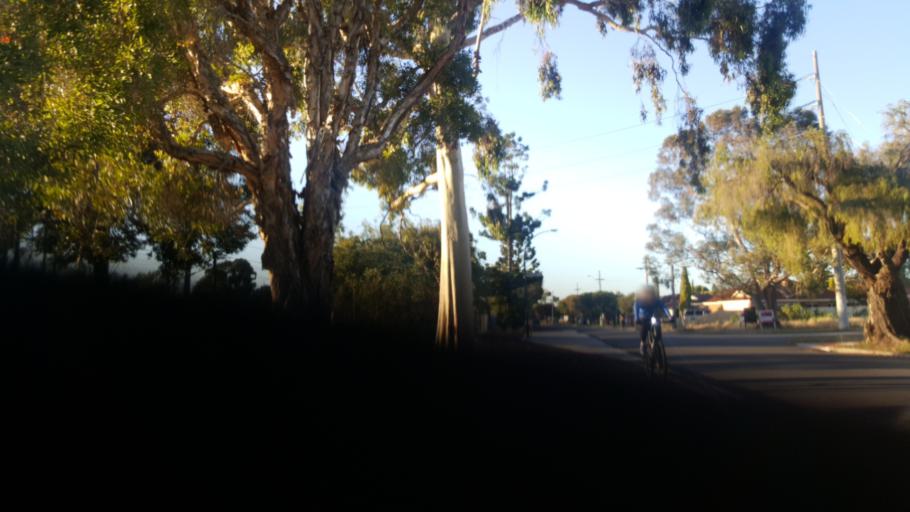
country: AU
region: Western Australia
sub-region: Victoria Park
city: East Victoria Park
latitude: -31.9859
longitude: 115.9155
